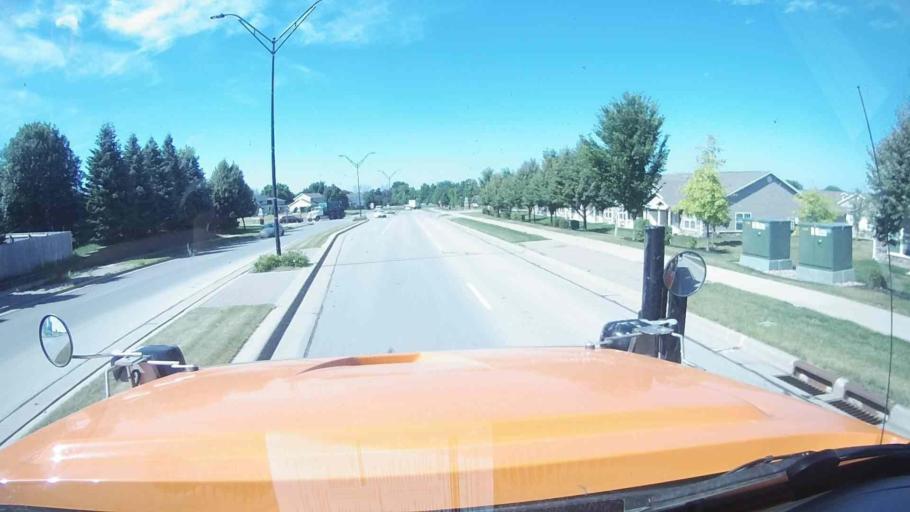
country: US
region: Iowa
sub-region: Polk County
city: Altoona
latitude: 41.6611
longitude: -93.4698
